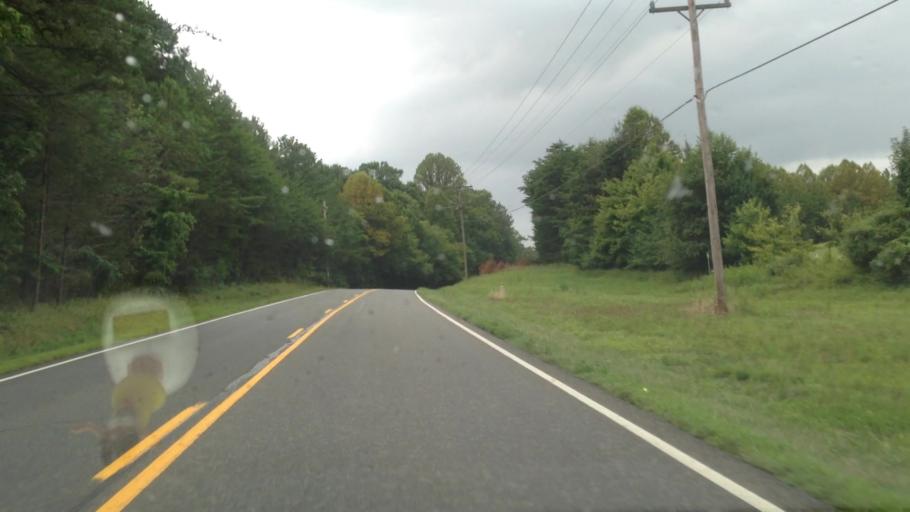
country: US
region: North Carolina
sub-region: Stokes County
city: Walnut Cove
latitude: 36.2808
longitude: -80.0791
